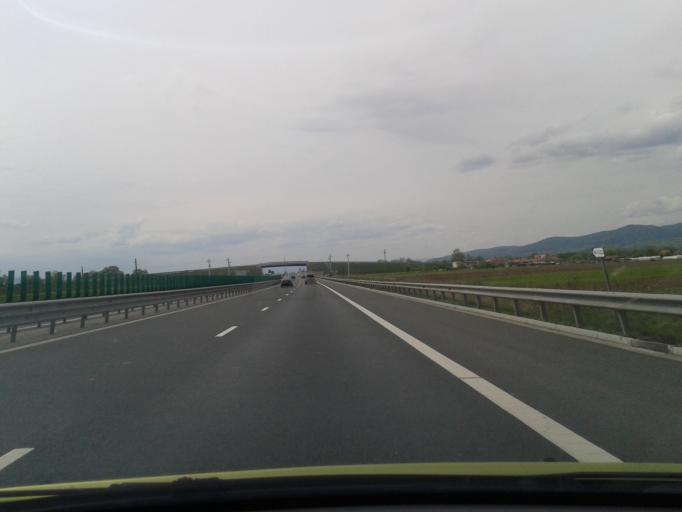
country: RO
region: Hunedoara
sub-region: Comuna Geoagiu
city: Geoagiu
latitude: 45.8889
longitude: 23.2504
